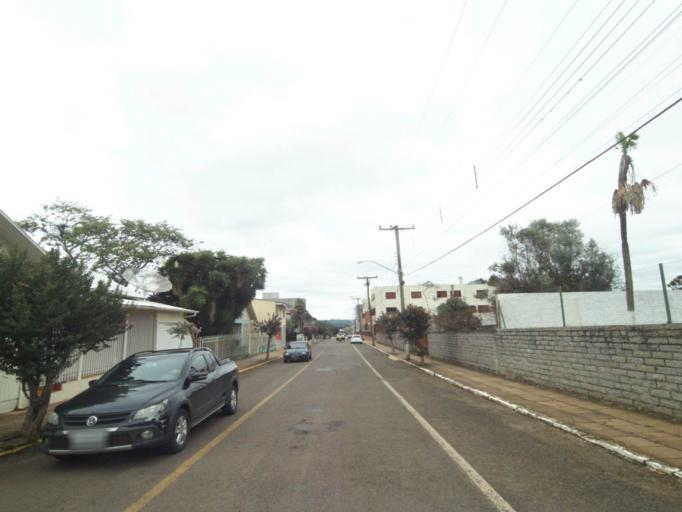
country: BR
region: Rio Grande do Sul
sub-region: Lagoa Vermelha
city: Lagoa Vermelha
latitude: -28.2107
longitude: -51.5279
